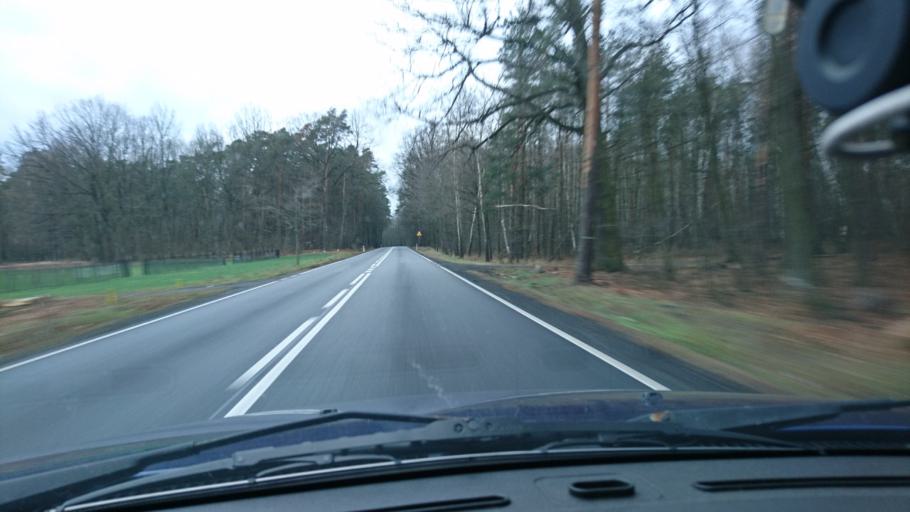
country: PL
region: Opole Voivodeship
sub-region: Powiat kluczborski
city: Kluczbork
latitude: 50.9422
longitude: 18.3242
